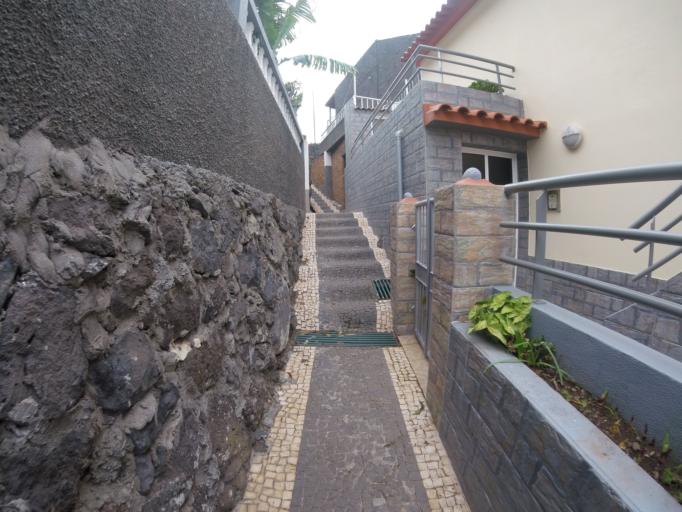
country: PT
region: Madeira
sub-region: Calheta
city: Estreito da Calheta
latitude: 32.7393
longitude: -17.2118
